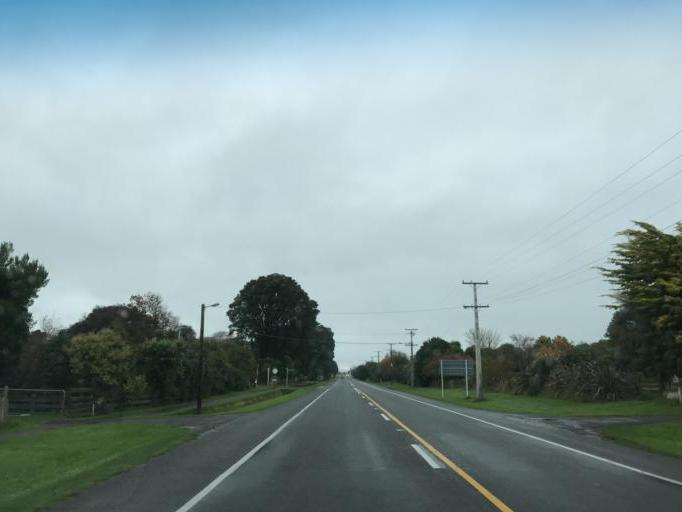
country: NZ
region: Taranaki
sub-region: South Taranaki District
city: Patea
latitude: -39.7648
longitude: 174.6243
